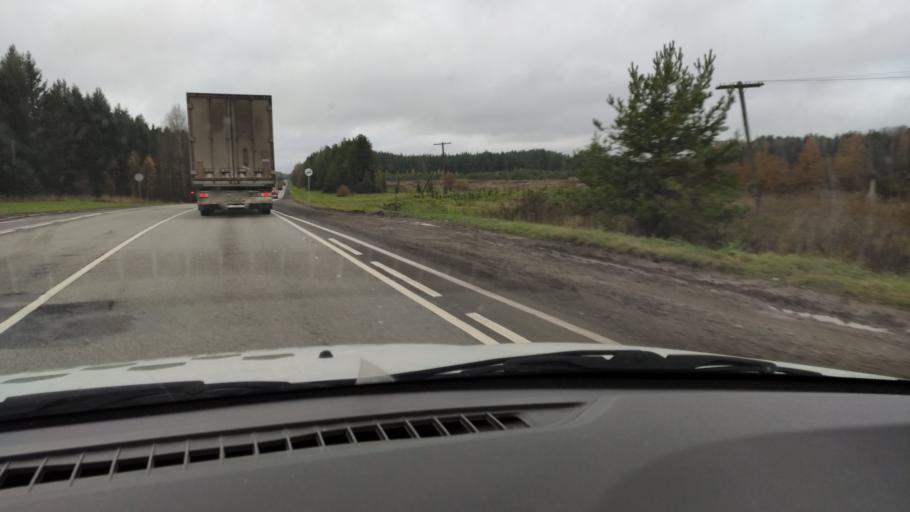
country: RU
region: Kirov
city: Belaya Kholunitsa
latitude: 58.8014
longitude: 50.5368
